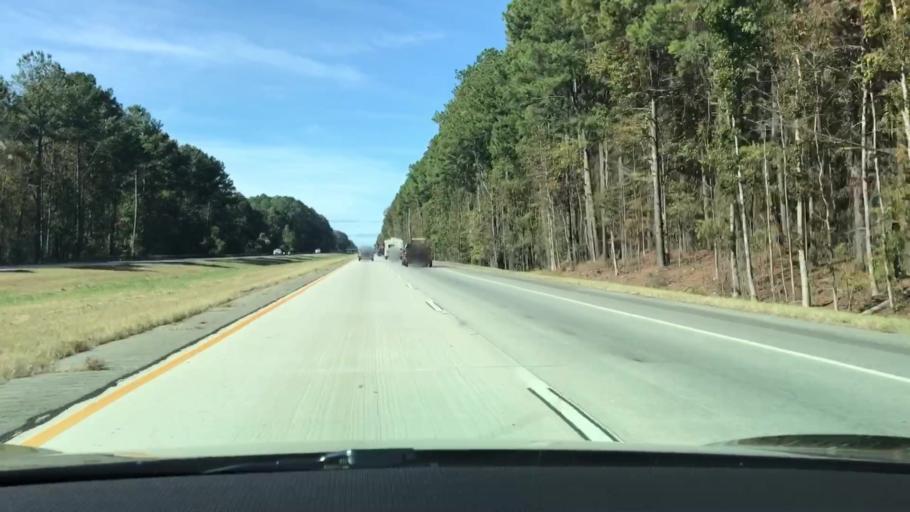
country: US
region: Georgia
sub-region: Greene County
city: Greensboro
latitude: 33.5488
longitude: -83.1513
